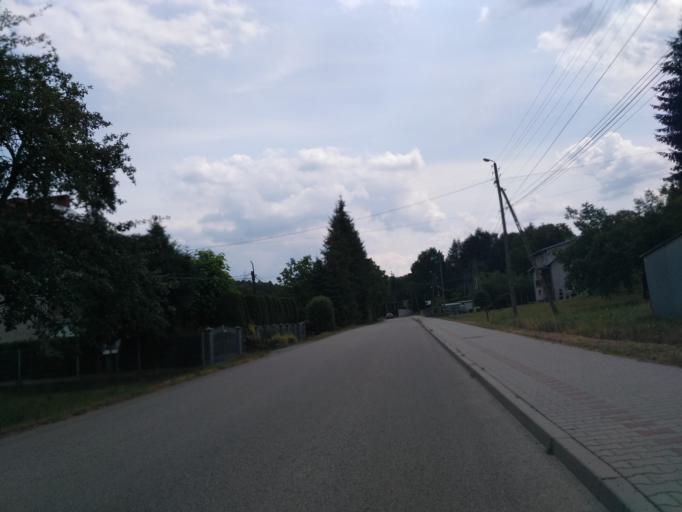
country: PL
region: Subcarpathian Voivodeship
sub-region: Powiat debicki
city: Brzeznica
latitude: 50.0434
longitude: 21.4906
